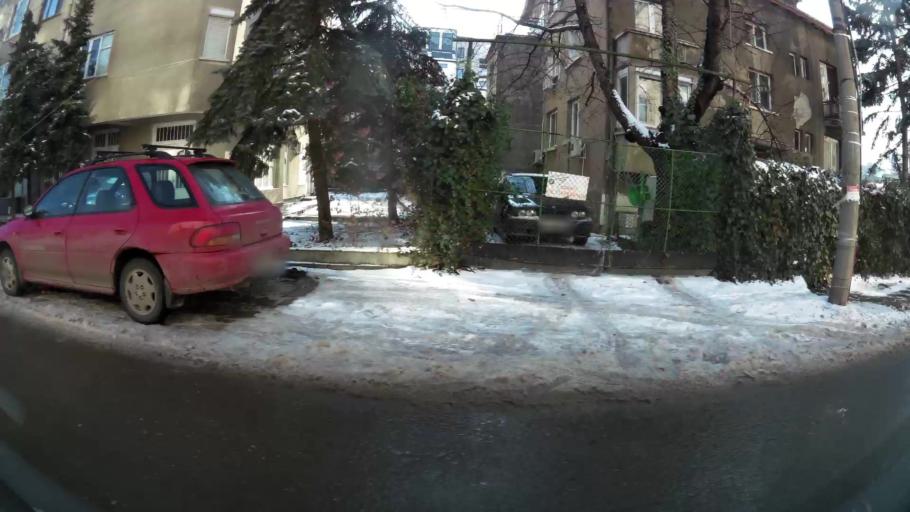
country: BG
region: Sofia-Capital
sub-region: Stolichna Obshtina
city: Sofia
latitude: 42.6670
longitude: 23.3492
